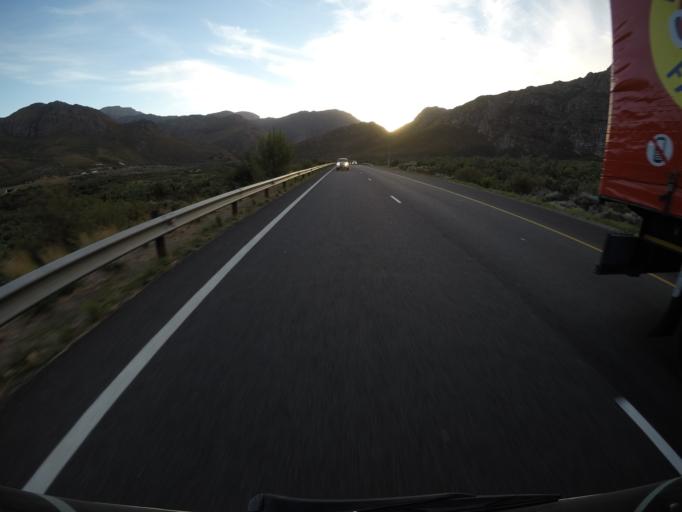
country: ZA
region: Western Cape
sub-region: Cape Winelands District Municipality
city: Paarl
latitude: -33.7261
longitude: 19.1308
